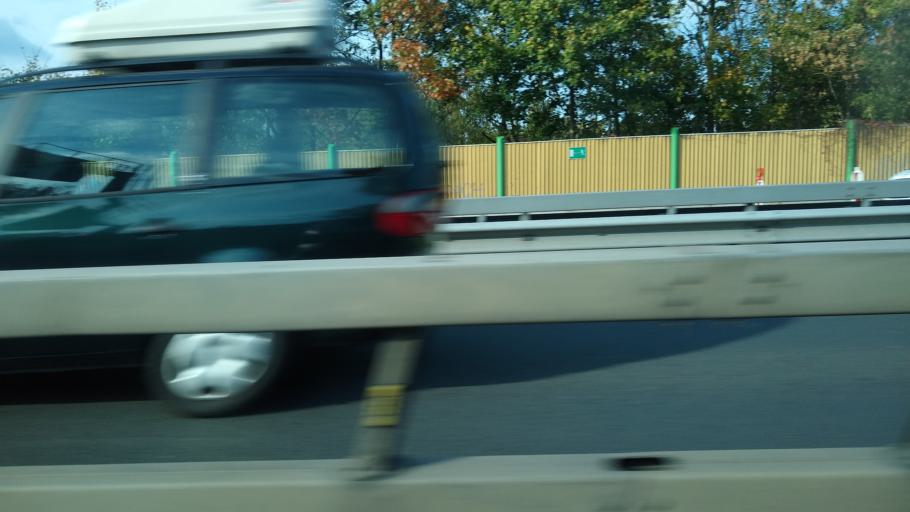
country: DE
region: Lower Saxony
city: Oldenburg
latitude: 53.1602
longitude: 8.2019
